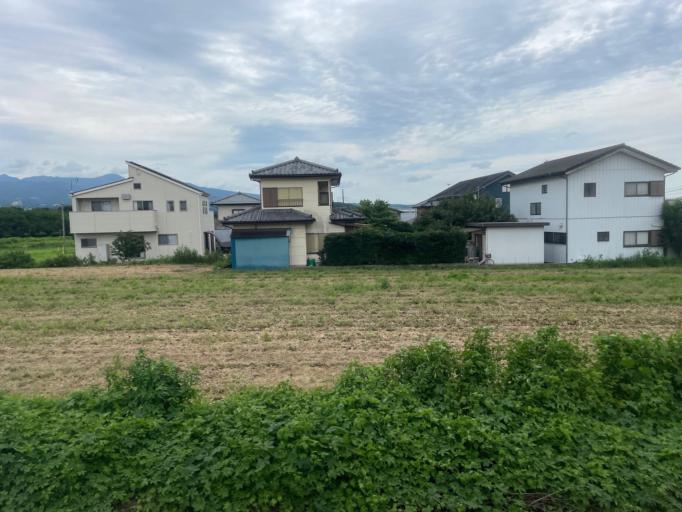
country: JP
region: Gunma
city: Shibukawa
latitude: 36.4492
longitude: 139.0202
